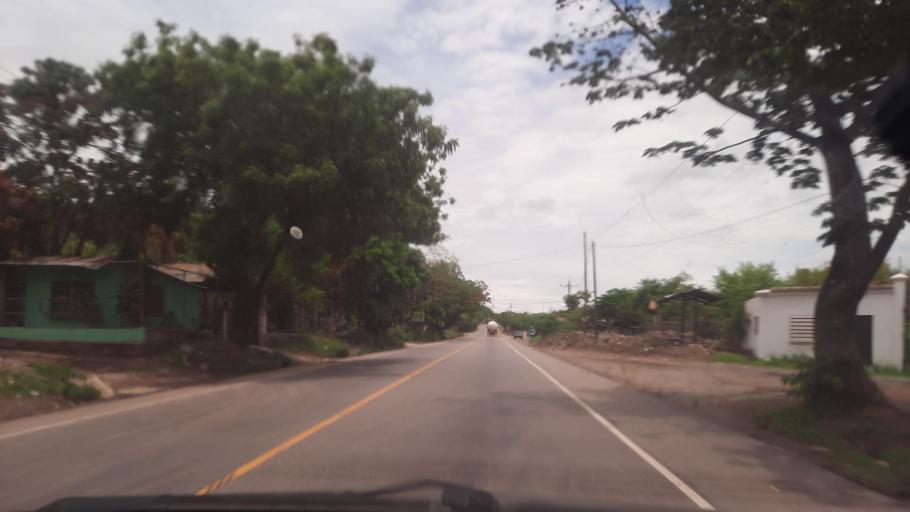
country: GT
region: Zacapa
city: Rio Hondo
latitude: 15.0791
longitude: -89.4892
